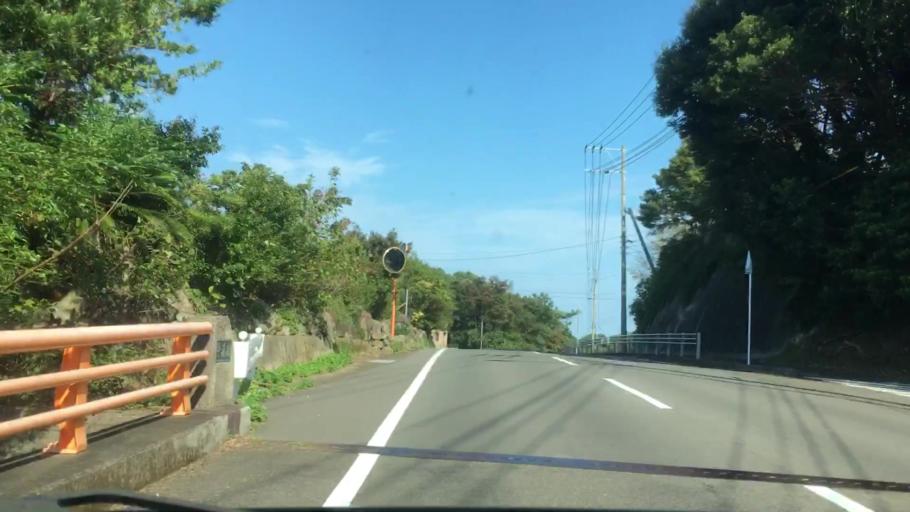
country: JP
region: Nagasaki
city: Sasebo
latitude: 33.0088
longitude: 129.6569
